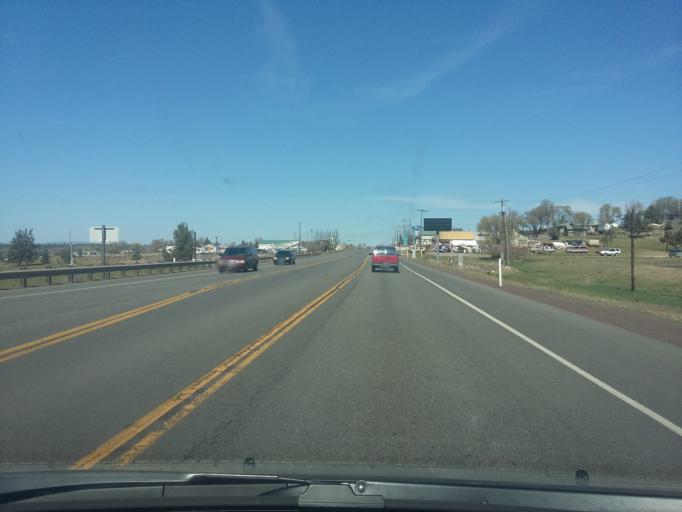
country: US
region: Oregon
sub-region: Jefferson County
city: Madras
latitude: 44.6081
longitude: -121.1386
